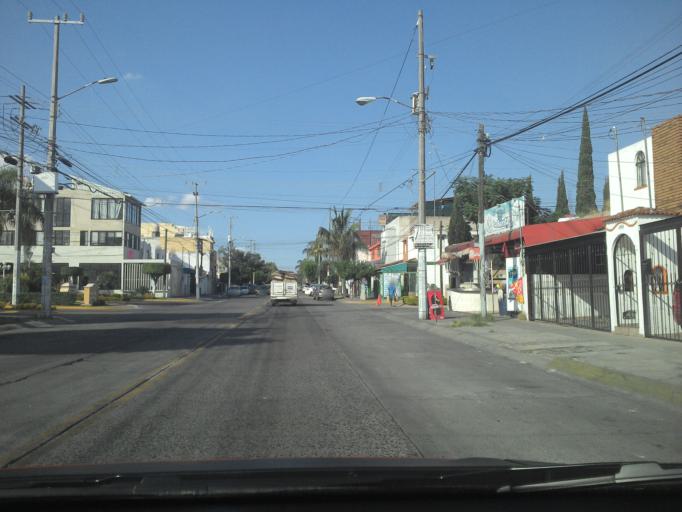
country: MX
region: Jalisco
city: Guadalajara
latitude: 20.6548
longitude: -103.4427
